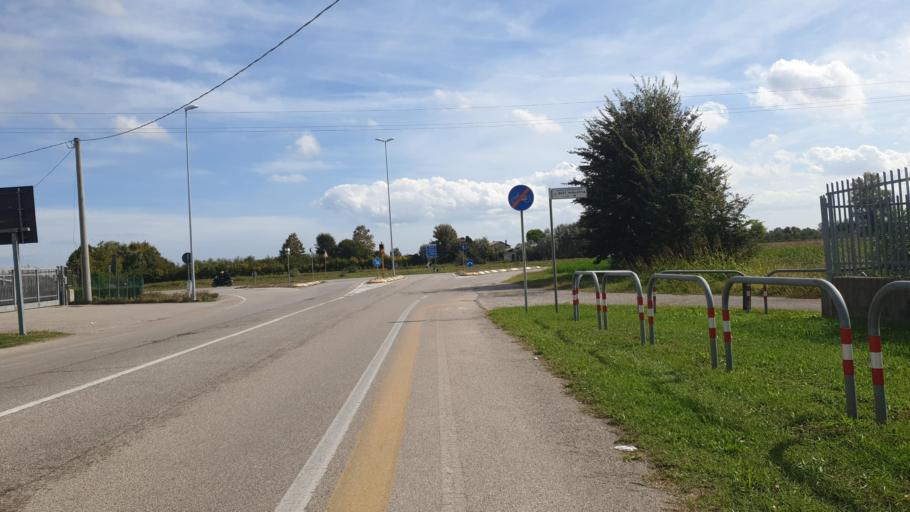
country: IT
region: Veneto
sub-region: Provincia di Padova
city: Arzergrande
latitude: 45.2818
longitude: 12.0516
